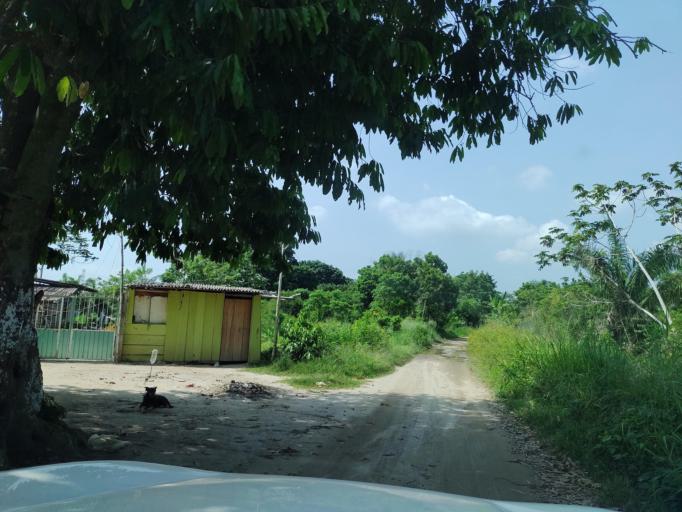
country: MX
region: Veracruz
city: Martinez de la Torre
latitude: 20.0899
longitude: -97.0498
